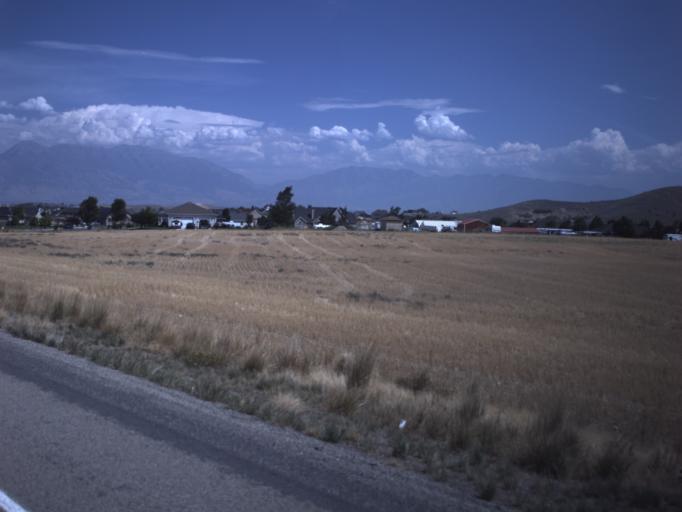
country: US
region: Utah
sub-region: Utah County
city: Eagle Mountain
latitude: 40.3716
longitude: -112.0230
